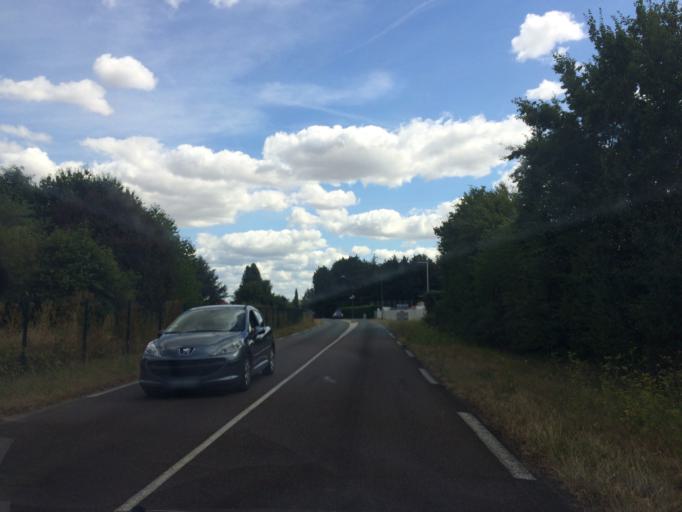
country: FR
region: Ile-de-France
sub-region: Departement de l'Essonne
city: Saint-Vrain
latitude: 48.5469
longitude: 2.3197
